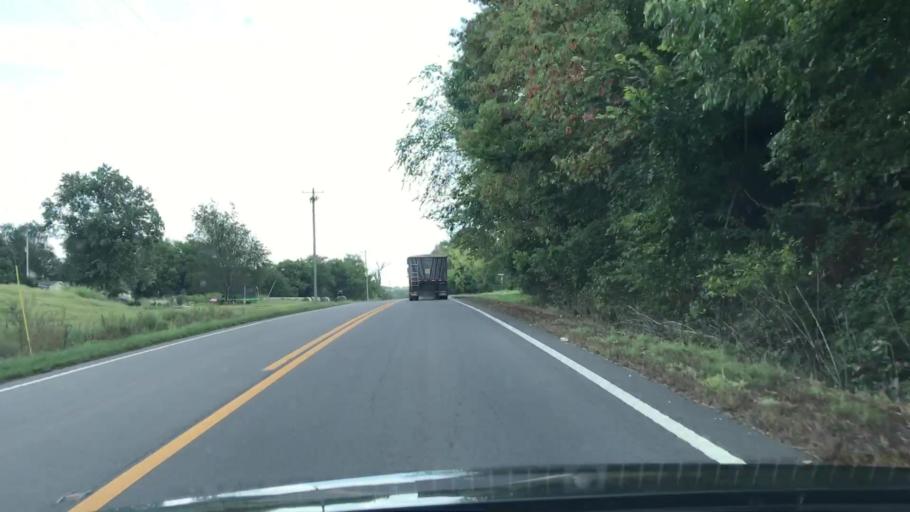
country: US
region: Tennessee
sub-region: Robertson County
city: Springfield
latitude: 36.6346
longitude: -86.9715
